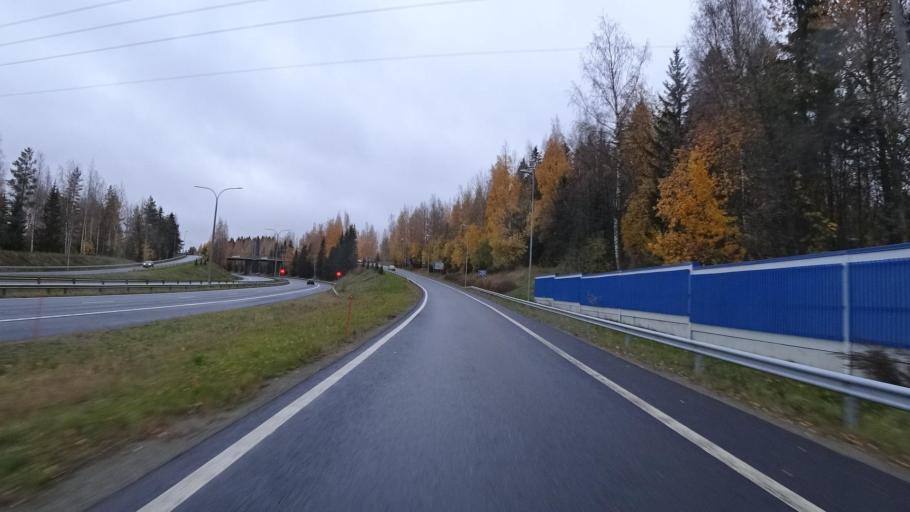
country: FI
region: Northern Savo
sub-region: Kuopio
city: Kuopio
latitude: 62.9370
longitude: 27.6660
